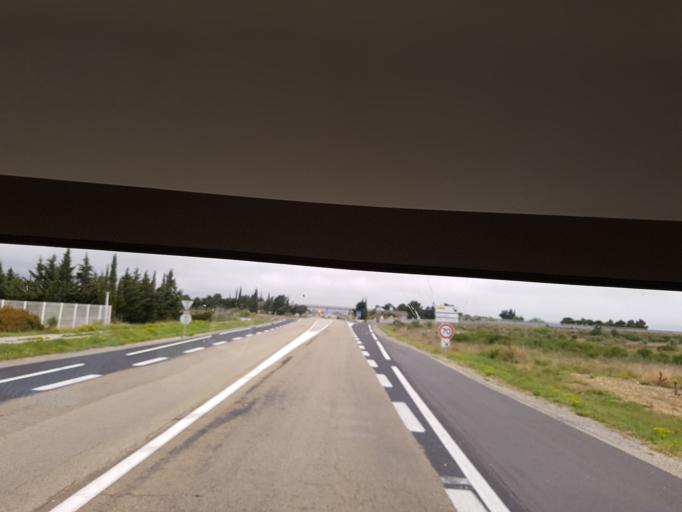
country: FR
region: Languedoc-Roussillon
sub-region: Departement de l'Aude
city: Leucate
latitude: 42.9338
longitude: 2.9921
